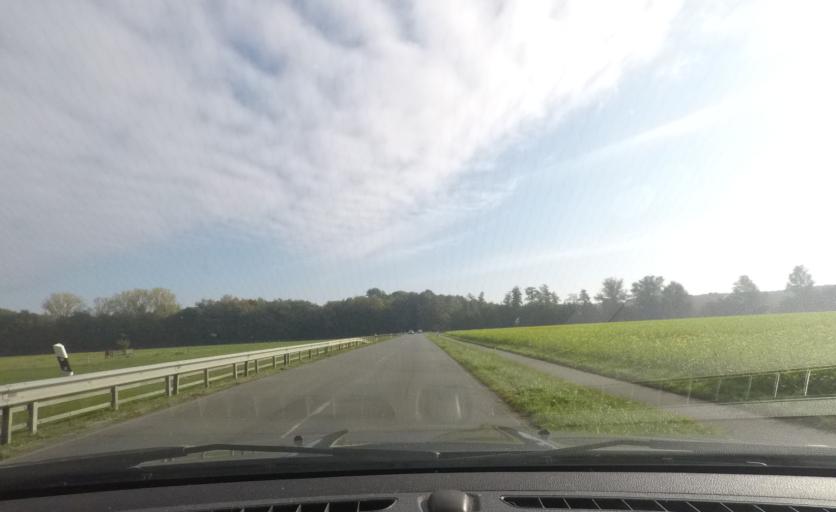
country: DE
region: North Rhine-Westphalia
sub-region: Regierungsbezirk Munster
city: Dulmen
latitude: 51.8497
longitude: 7.2133
